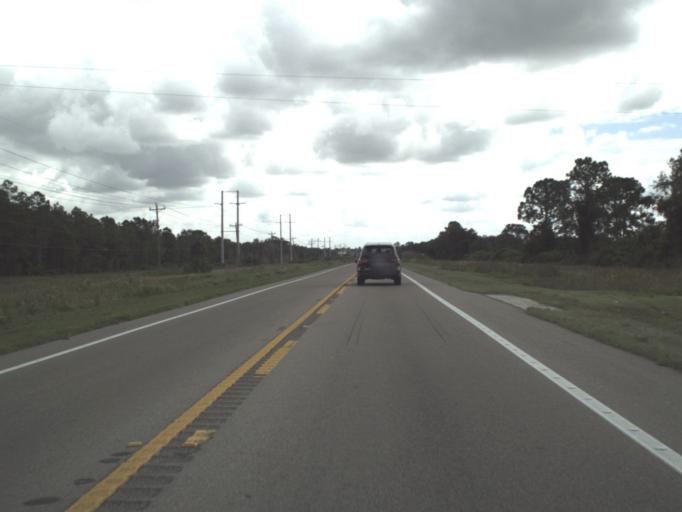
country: US
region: Florida
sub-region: Lee County
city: Gateway
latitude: 26.5644
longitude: -81.6738
